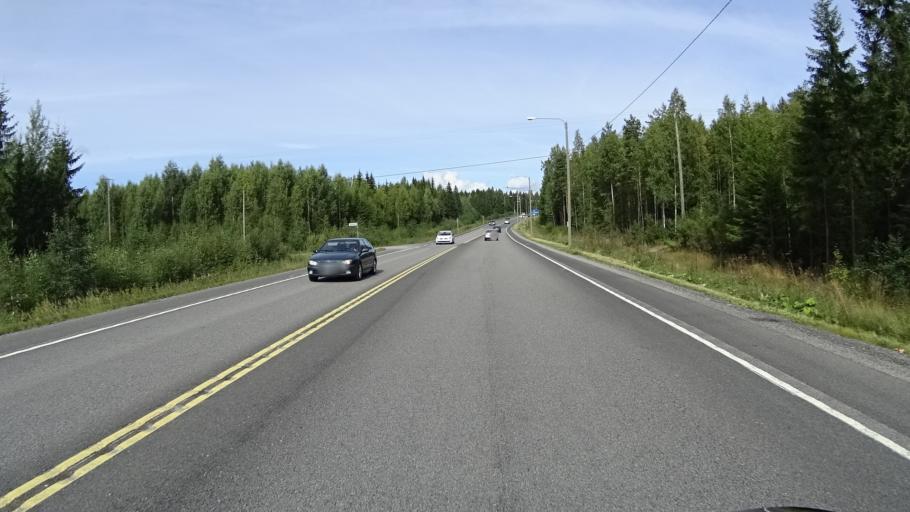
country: FI
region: Pirkanmaa
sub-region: Tampere
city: Haemeenkyroe
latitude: 61.6709
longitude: 23.1590
